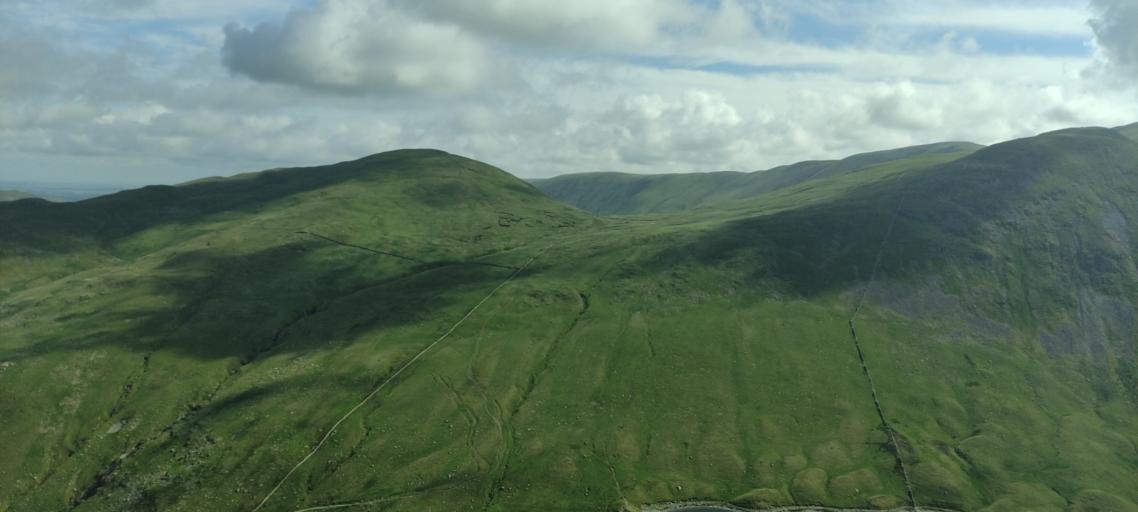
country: GB
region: England
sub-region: Cumbria
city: Ambleside
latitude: 54.5020
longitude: -2.8896
